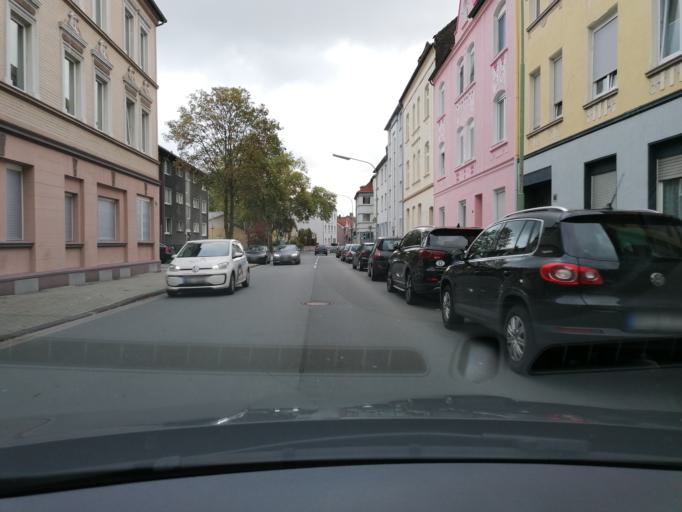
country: DE
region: North Rhine-Westphalia
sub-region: Regierungsbezirk Munster
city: Gelsenkirchen
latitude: 51.5377
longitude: 7.1526
